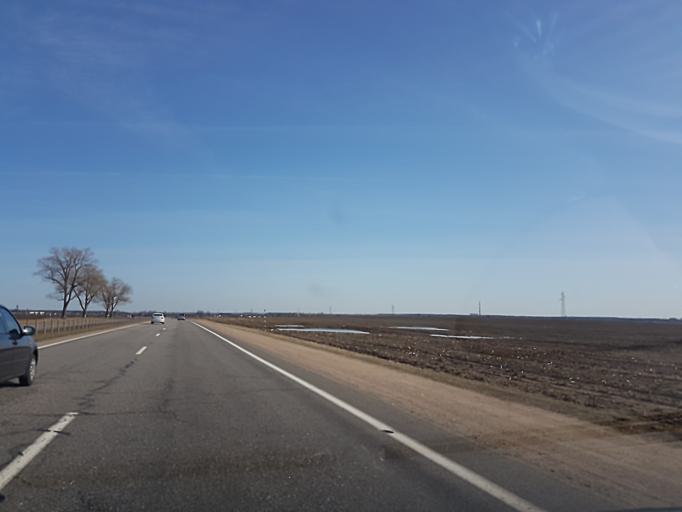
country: BY
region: Minsk
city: Dukora
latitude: 53.6823
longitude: 27.9187
